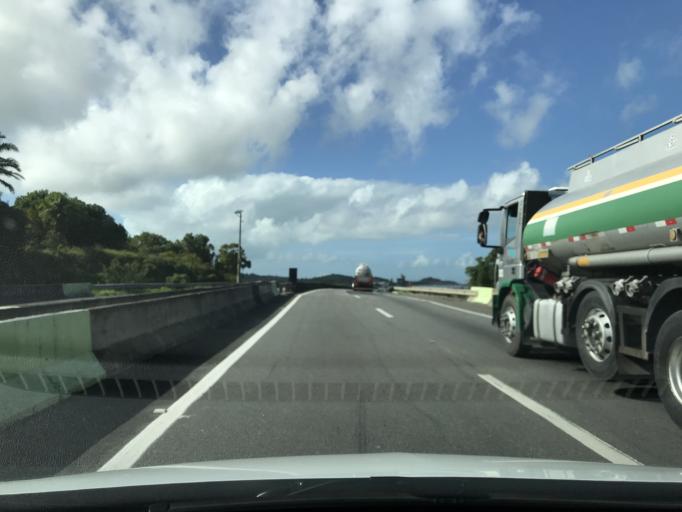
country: BR
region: Pernambuco
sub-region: Cabo De Santo Agostinho
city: Cabo
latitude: -8.3128
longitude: -35.0004
